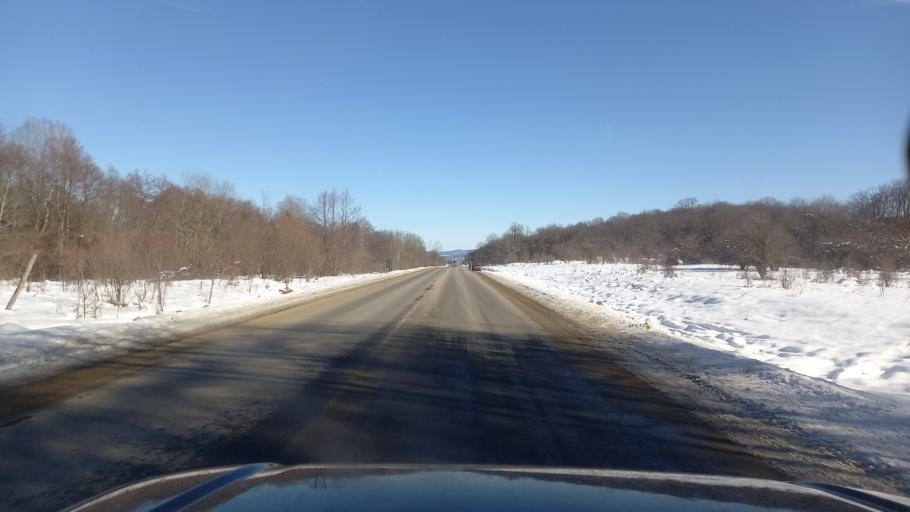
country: RU
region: Adygeya
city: Kamennomostskiy
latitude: 44.2188
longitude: 40.0846
